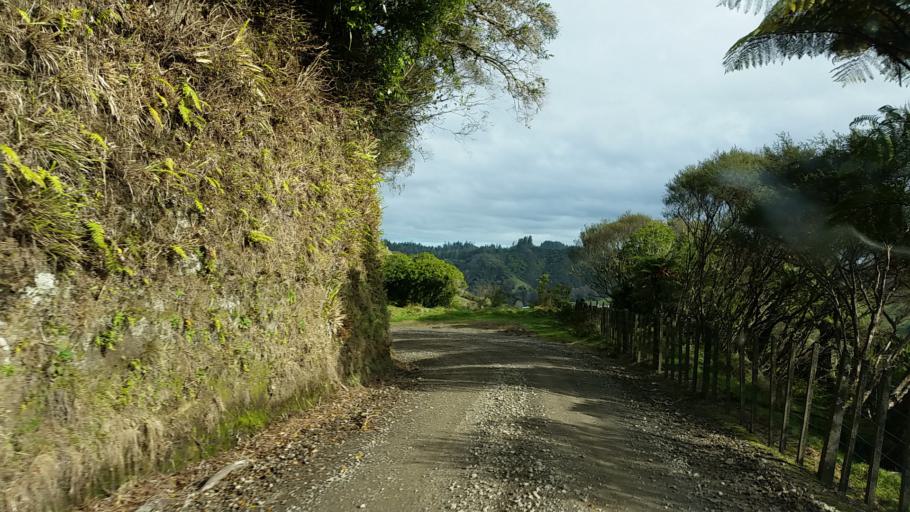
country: NZ
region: Taranaki
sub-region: South Taranaki District
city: Eltham
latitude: -39.1752
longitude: 174.6281
